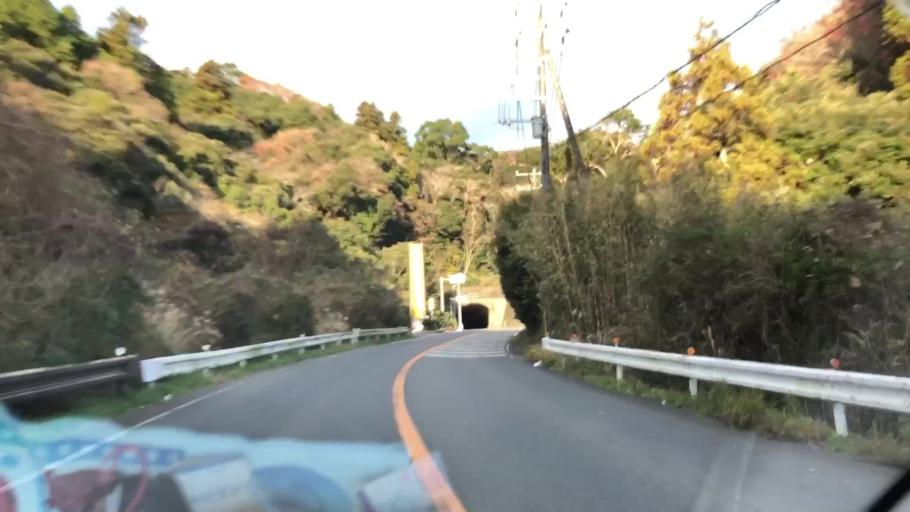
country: JP
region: Chiba
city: Tateyama
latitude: 34.9873
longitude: 139.9325
